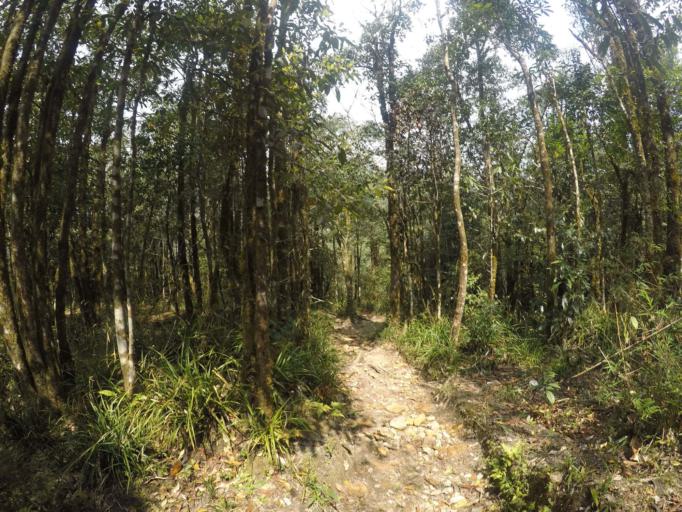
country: VN
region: Lao Cai
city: Sa Pa
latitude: 22.3492
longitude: 103.7743
